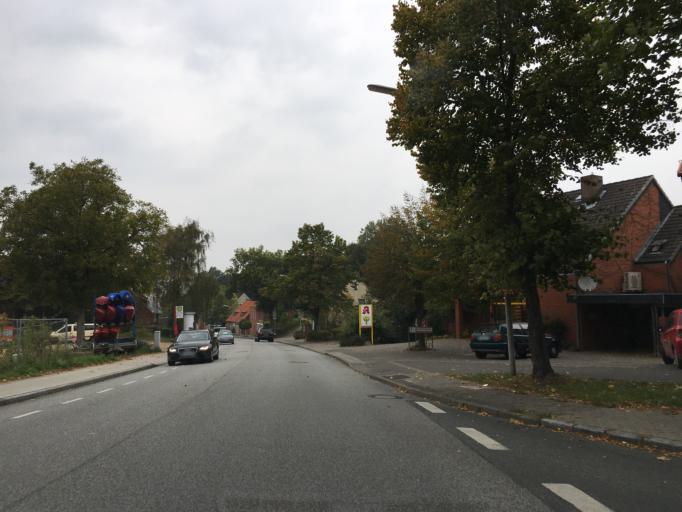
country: DE
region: Schleswig-Holstein
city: Ratzeburg
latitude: 53.6937
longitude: 10.7868
